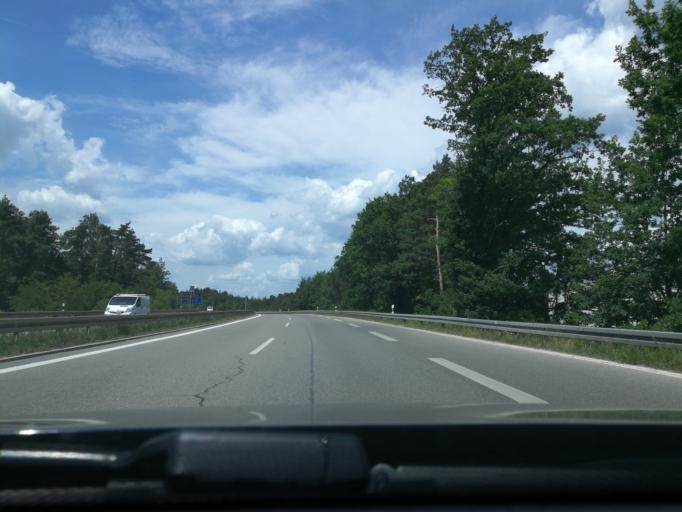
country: DE
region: Bavaria
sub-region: Regierungsbezirk Mittelfranken
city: Feucht
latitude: 49.3662
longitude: 11.2046
